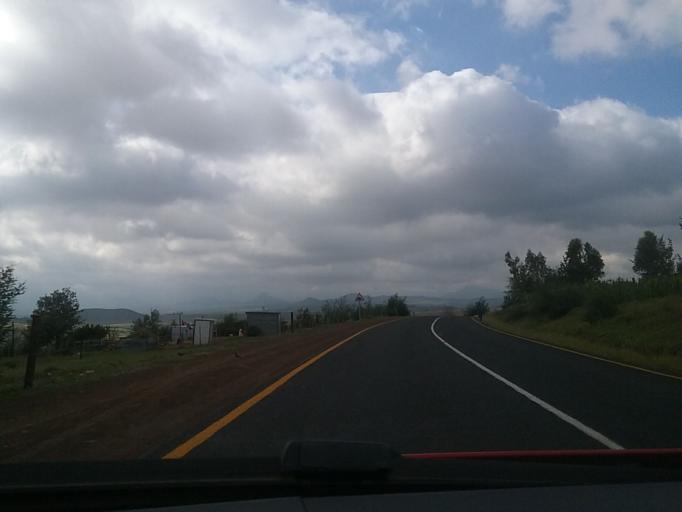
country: LS
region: Berea
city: Teyateyaneng
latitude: -29.1798
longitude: 27.7981
